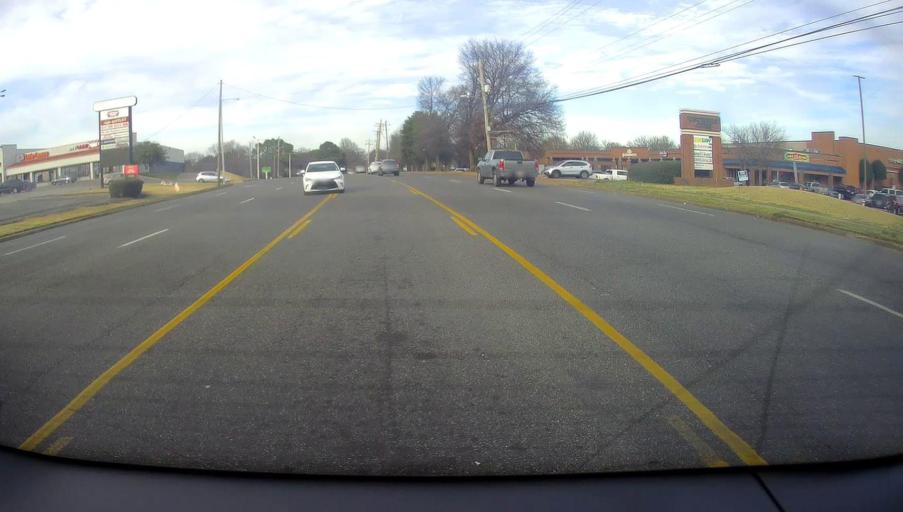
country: US
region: Tennessee
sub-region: Shelby County
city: Germantown
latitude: 35.0505
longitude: -89.8438
